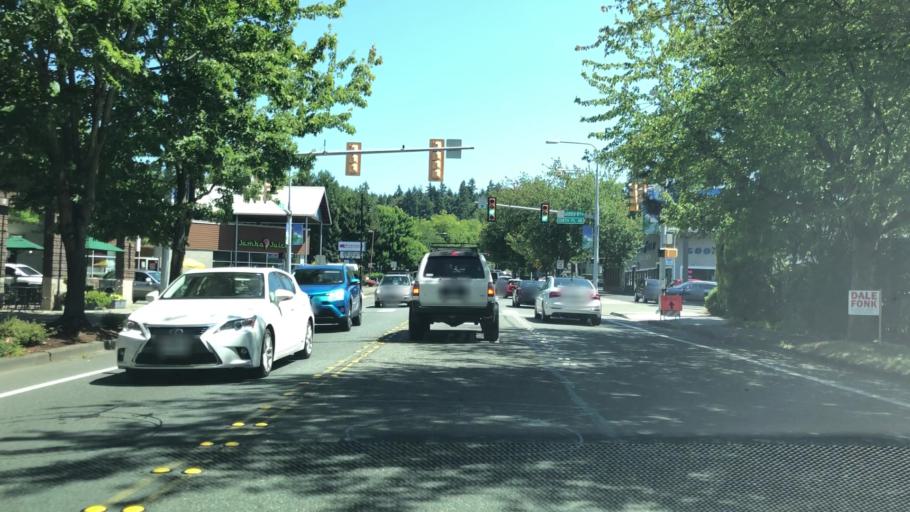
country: US
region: Washington
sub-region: King County
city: Woodinville
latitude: 47.7545
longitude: -122.1558
